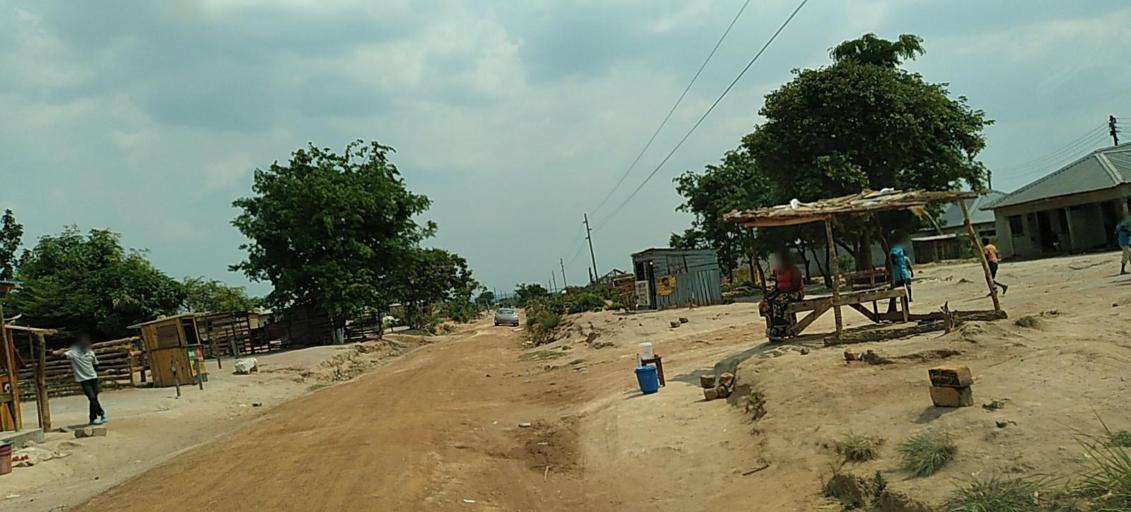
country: ZM
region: Copperbelt
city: Kalulushi
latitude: -12.8584
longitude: 28.0782
